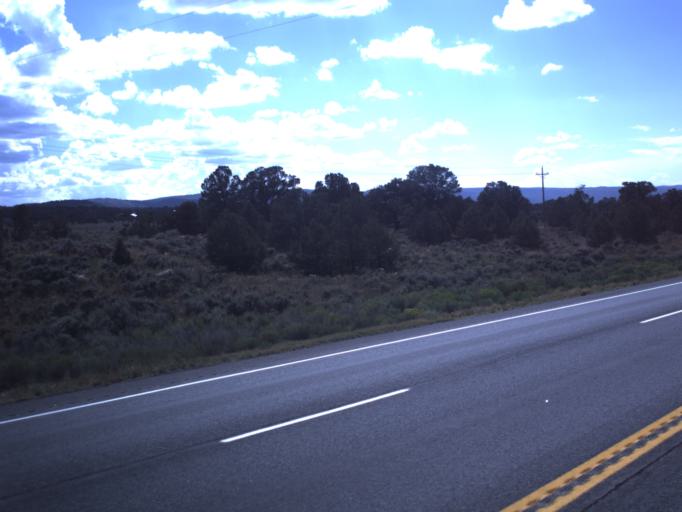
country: US
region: Utah
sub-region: Duchesne County
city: Duchesne
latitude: 40.2022
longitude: -110.7098
